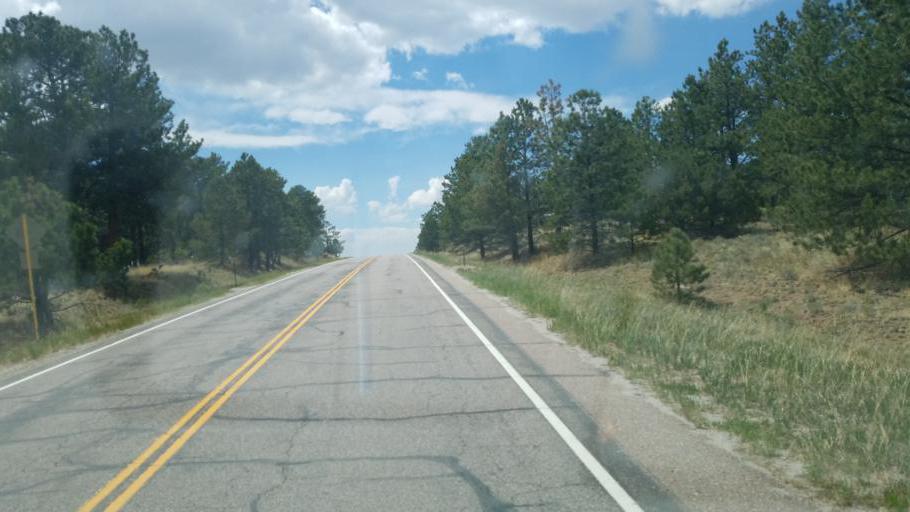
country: US
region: Colorado
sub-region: Custer County
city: Westcliffe
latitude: 38.1609
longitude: -105.2633
